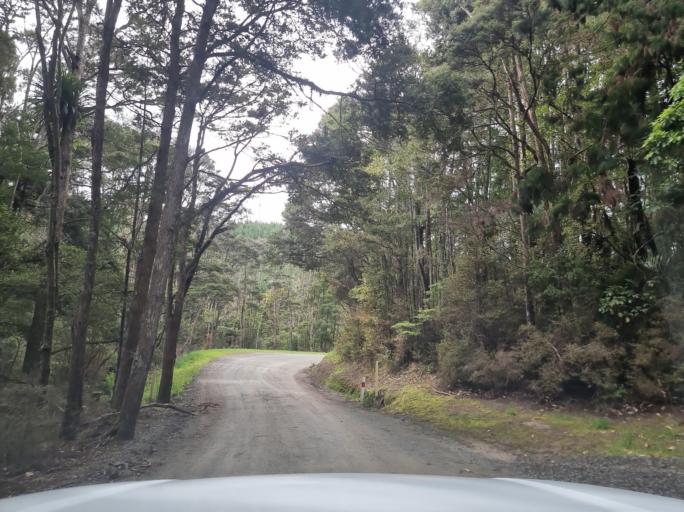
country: NZ
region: Northland
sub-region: Whangarei
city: Ruakaka
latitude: -36.1013
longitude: 174.2063
